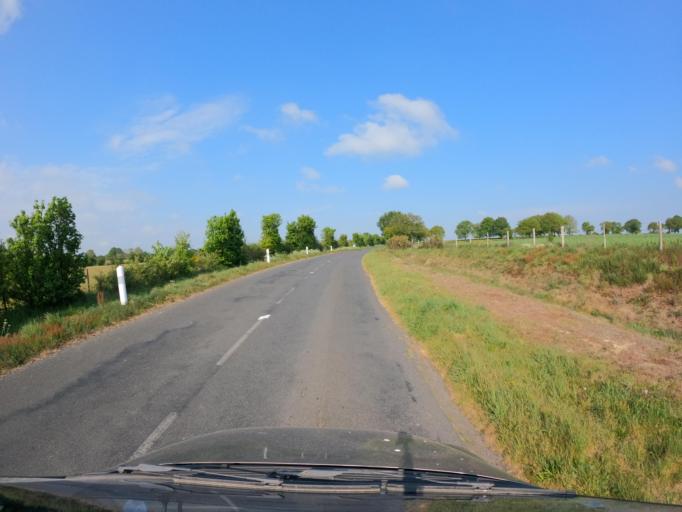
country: FR
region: Pays de la Loire
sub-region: Departement de Maine-et-Loire
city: Roussay
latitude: 47.0719
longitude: -1.0543
